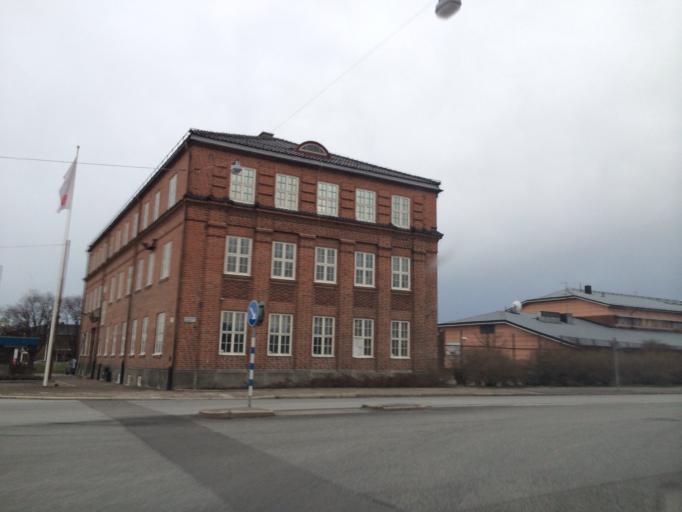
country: SE
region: Skane
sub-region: Malmo
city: Malmoe
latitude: 55.6131
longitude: 13.0143
